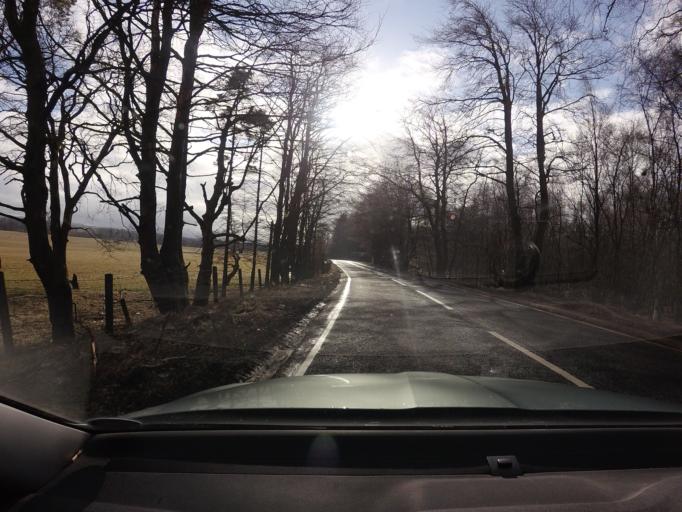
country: GB
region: Scotland
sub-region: South Lanarkshire
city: Forth
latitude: 55.7037
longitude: -3.7192
